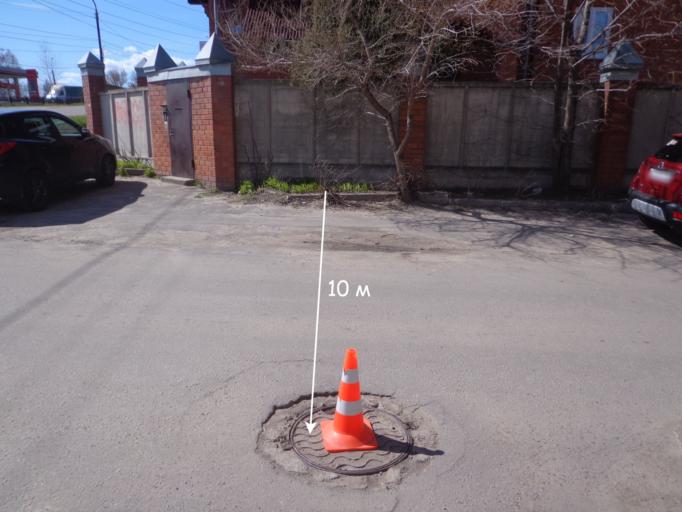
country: RU
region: Voronezj
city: Voronezh
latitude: 51.6906
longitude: 39.2230
